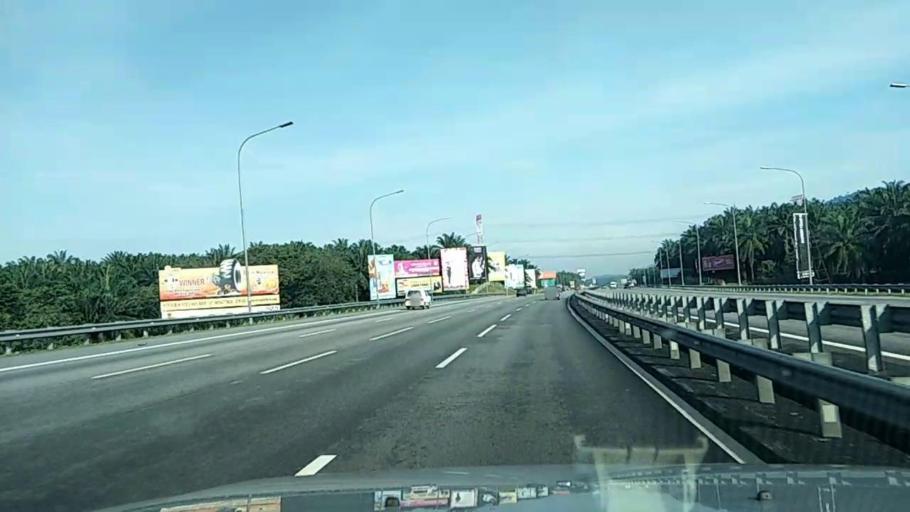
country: MY
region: Negeri Sembilan
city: Seremban
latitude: 2.7440
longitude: 101.8719
